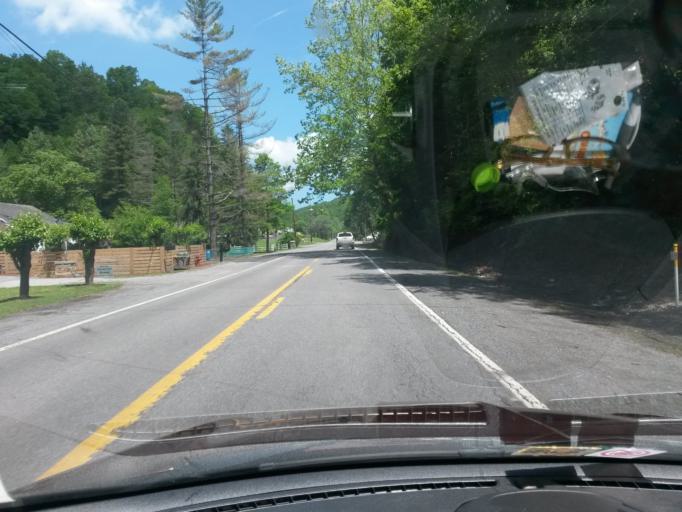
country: US
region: West Virginia
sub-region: McDowell County
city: Welch
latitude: 37.4642
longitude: -81.5409
